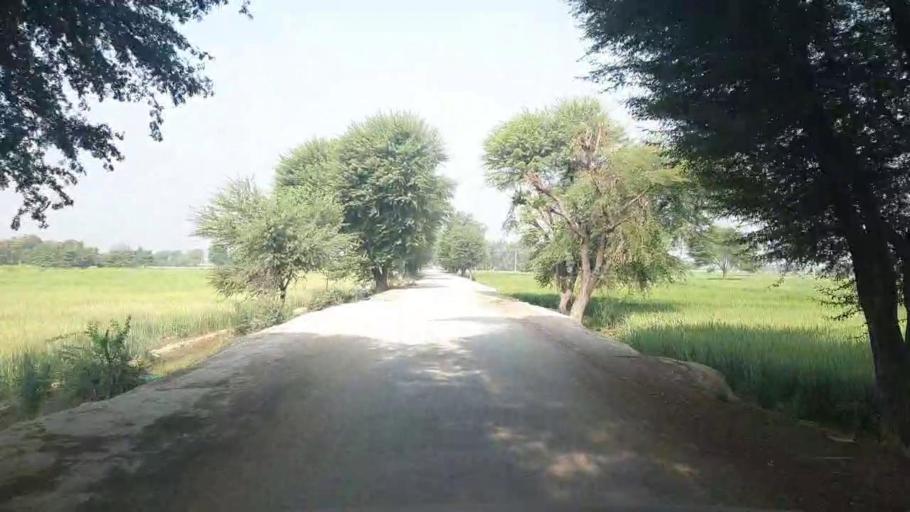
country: PK
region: Sindh
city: Umarkot
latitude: 25.3751
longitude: 69.7281
